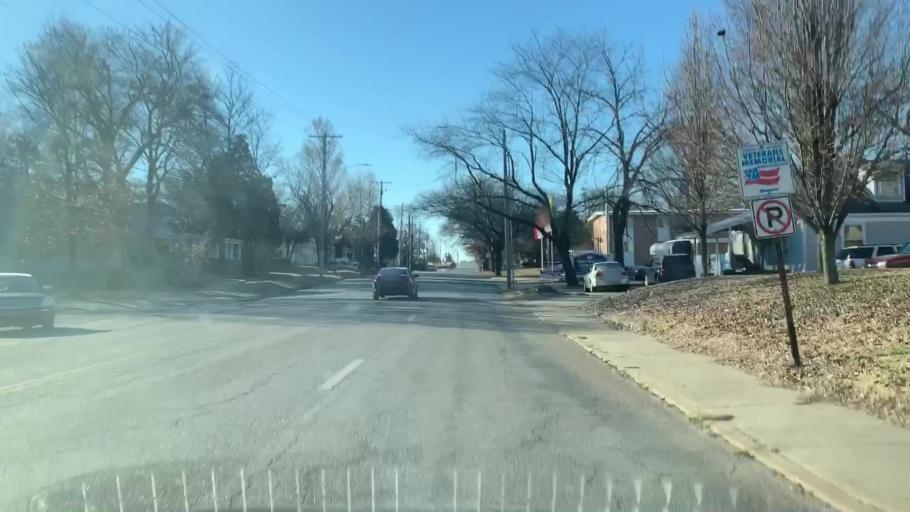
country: US
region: Kansas
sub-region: Crawford County
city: Pittsburg
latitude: 37.3894
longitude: -94.7052
